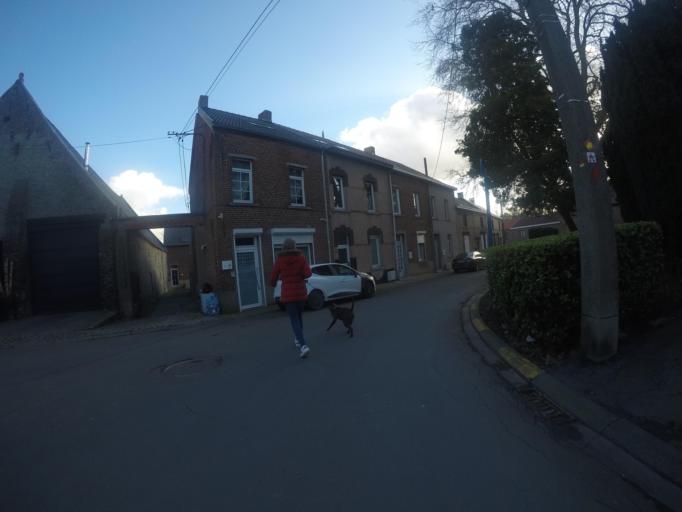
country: BE
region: Wallonia
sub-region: Province du Brabant Wallon
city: Tubize
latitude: 50.7043
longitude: 4.1608
